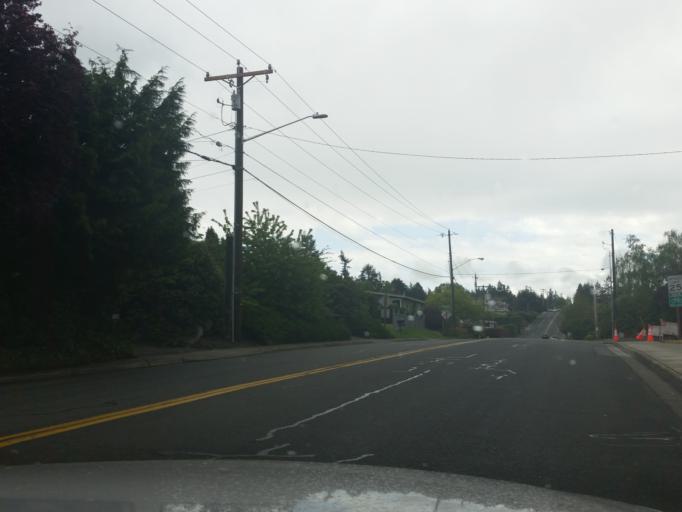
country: US
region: Washington
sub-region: Snohomish County
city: Edmonds
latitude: 47.8176
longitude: -122.3672
